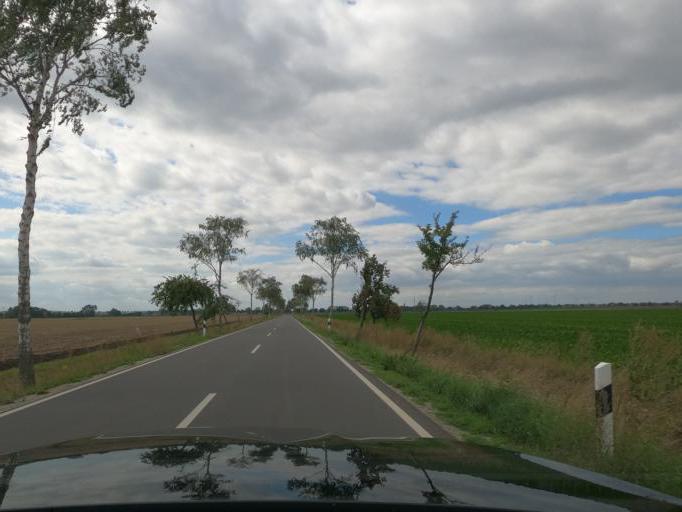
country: DE
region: Lower Saxony
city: Hohenhameln
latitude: 52.2271
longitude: 10.0820
